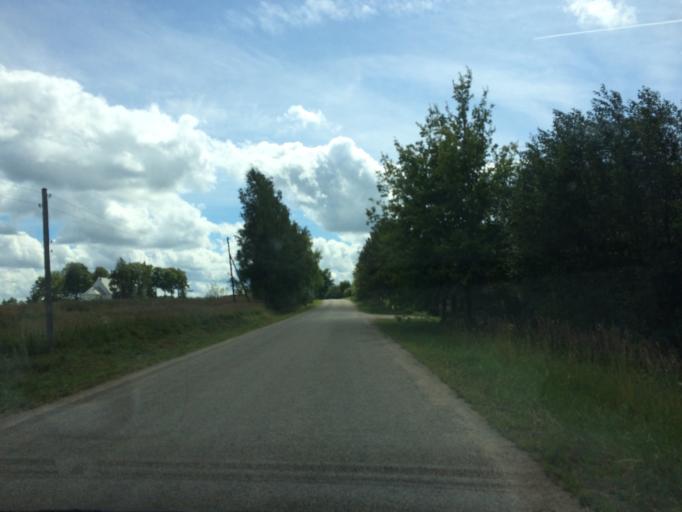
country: LV
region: Ludzas Rajons
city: Ludza
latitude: 56.6351
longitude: 27.5107
